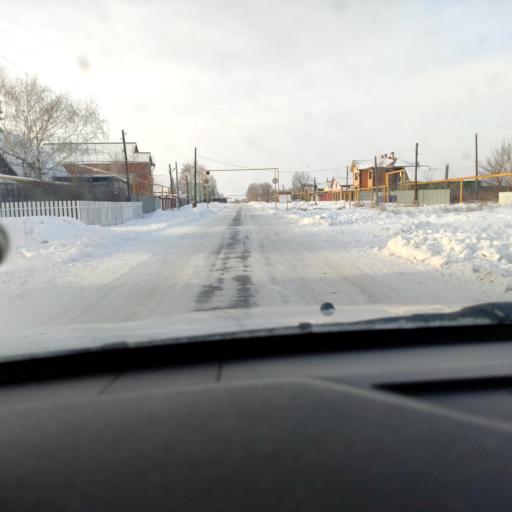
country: RU
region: Samara
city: Smyshlyayevka
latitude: 53.1651
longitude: 50.3884
